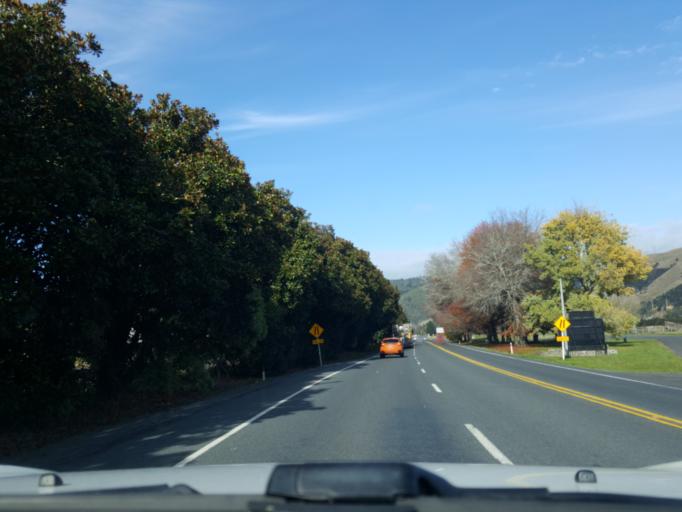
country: NZ
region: Waikato
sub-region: Waikato District
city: Ngaruawahia
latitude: -37.5837
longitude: 175.1595
